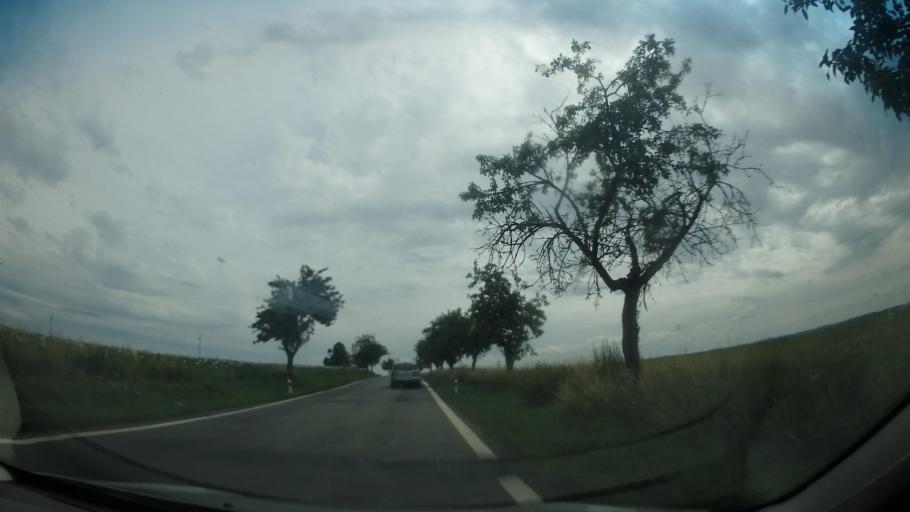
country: CZ
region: Vysocina
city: Bystrice nad Pernstejnem
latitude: 49.5003
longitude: 16.1739
